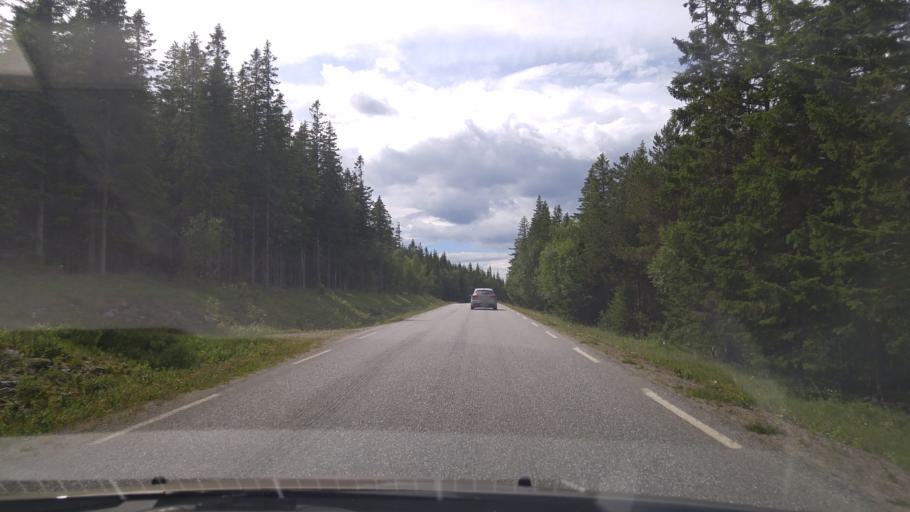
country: NO
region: Nord-Trondelag
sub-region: Naeroy
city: Kolvereid
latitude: 64.7231
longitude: 11.4973
